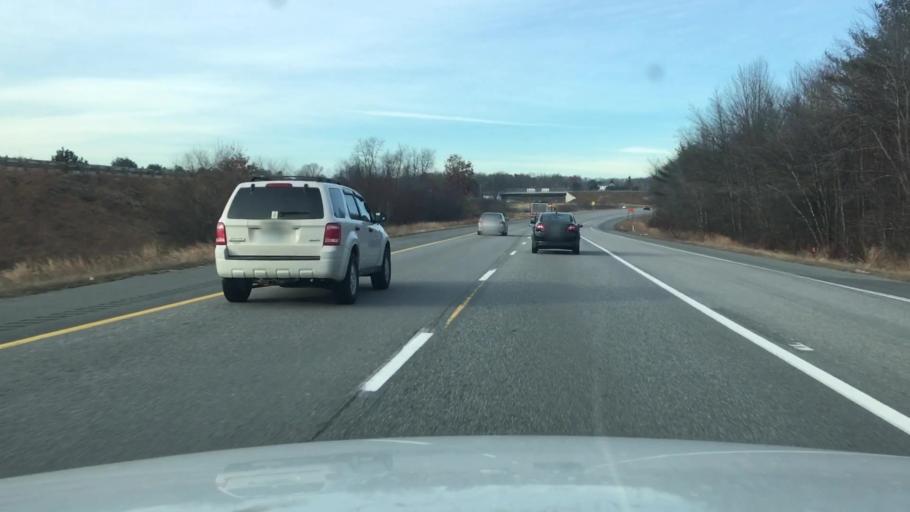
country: US
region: New Hampshire
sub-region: Hillsborough County
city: Manchester
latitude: 42.9645
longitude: -71.4111
